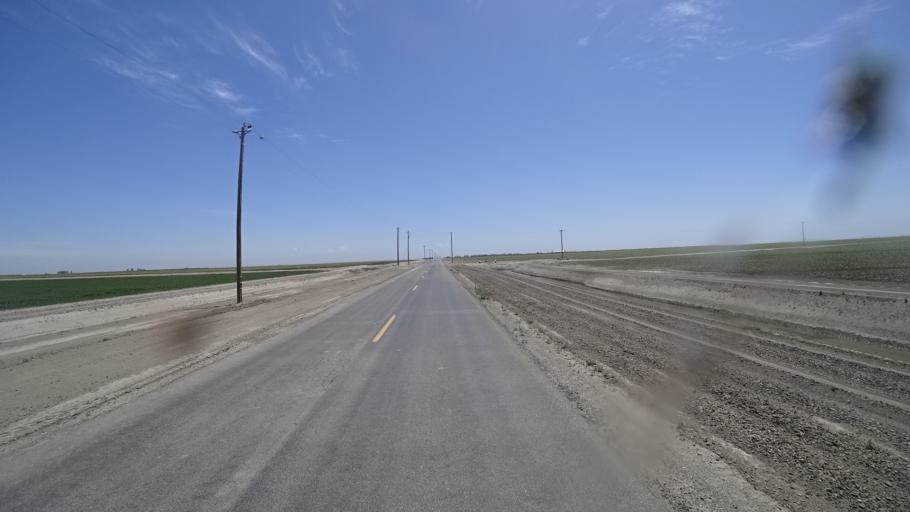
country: US
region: California
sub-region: Kings County
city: Corcoran
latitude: 36.1161
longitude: -119.6726
